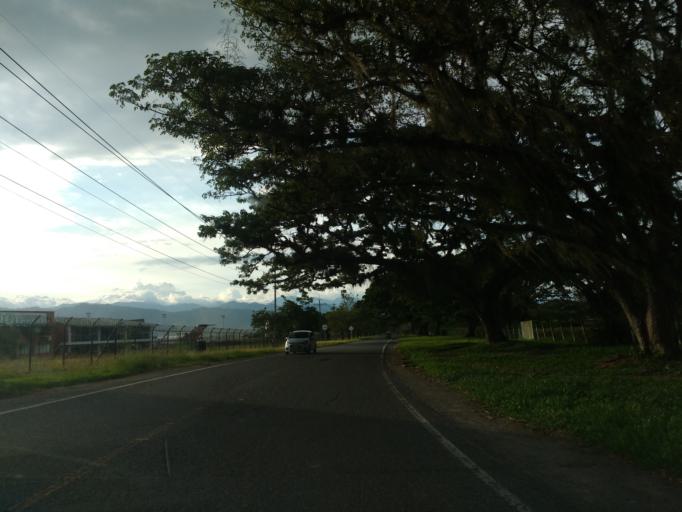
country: CO
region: Valle del Cauca
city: Cartago
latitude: 4.7600
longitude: -75.9514
